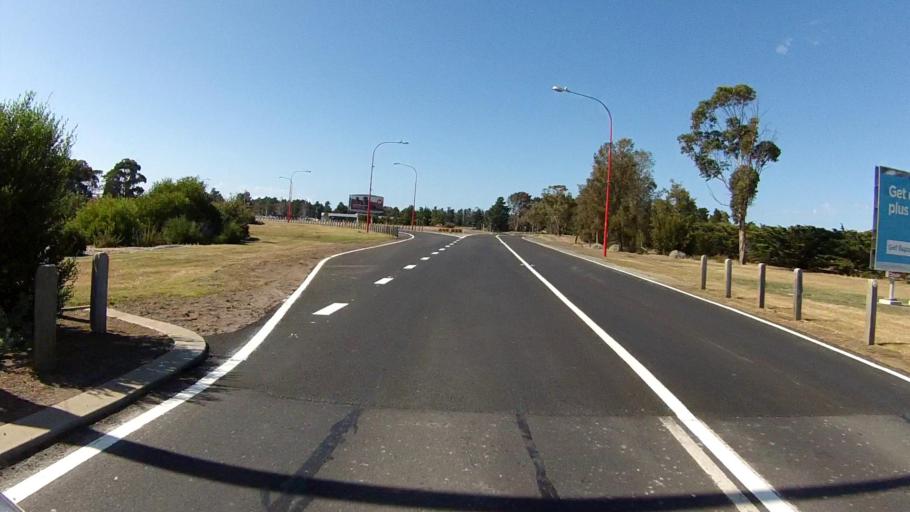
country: AU
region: Tasmania
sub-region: Clarence
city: Seven Mile Beach
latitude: -42.8382
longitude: 147.4991
